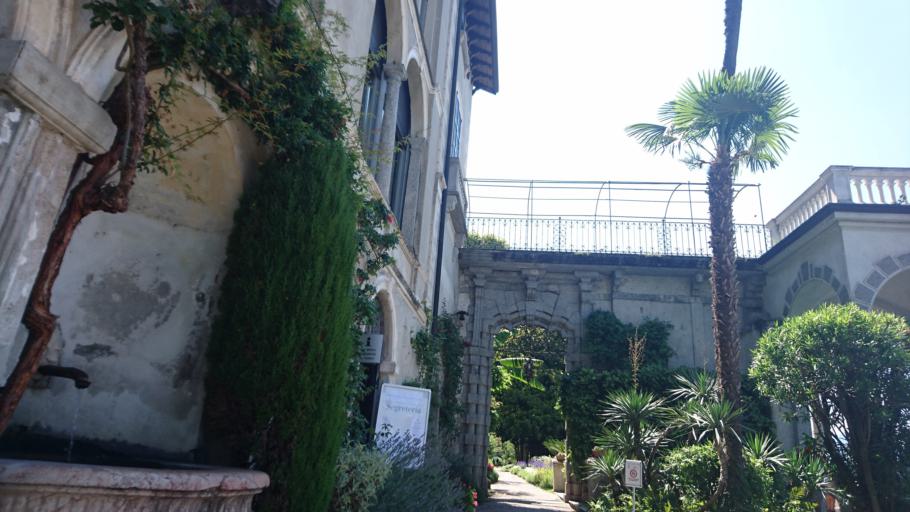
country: IT
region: Lombardy
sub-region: Provincia di Lecco
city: Varenna
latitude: 46.0079
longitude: 9.2878
